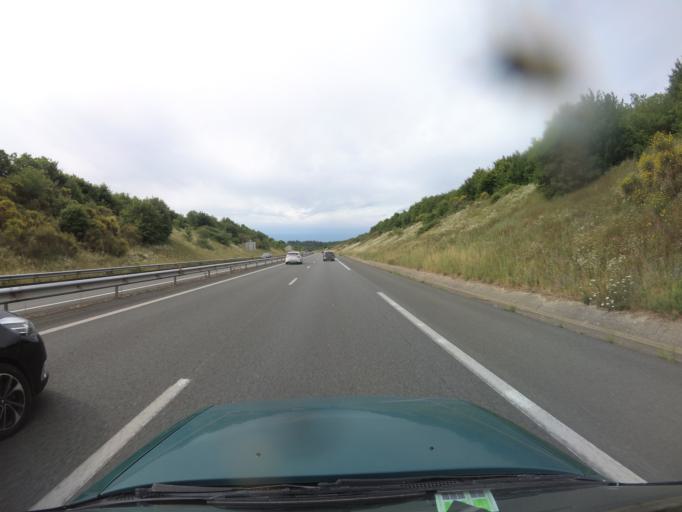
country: FR
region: Pays de la Loire
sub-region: Departement de la Vendee
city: Sainte-Hermine
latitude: 46.5793
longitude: -1.1170
